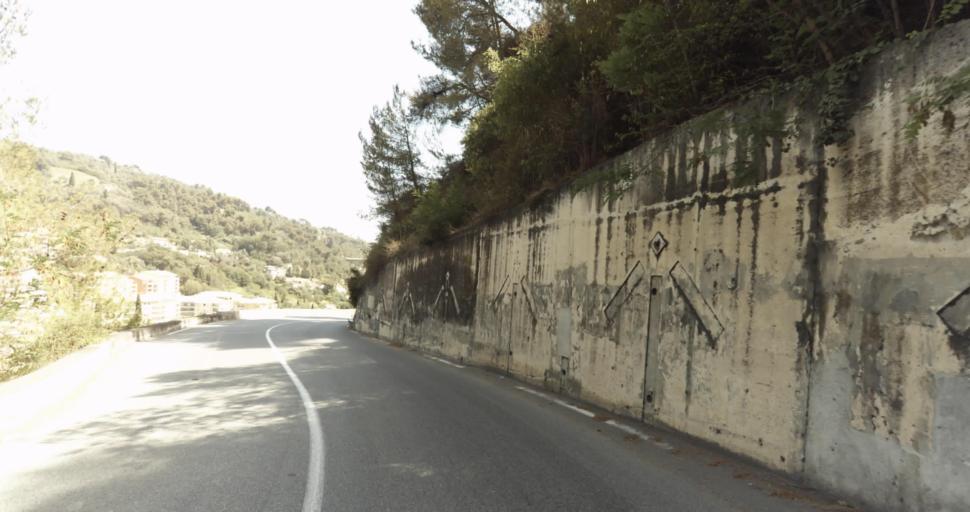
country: FR
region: Provence-Alpes-Cote d'Azur
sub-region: Departement des Alpes-Maritimes
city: Sainte-Agnes
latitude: 43.8013
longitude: 7.4857
